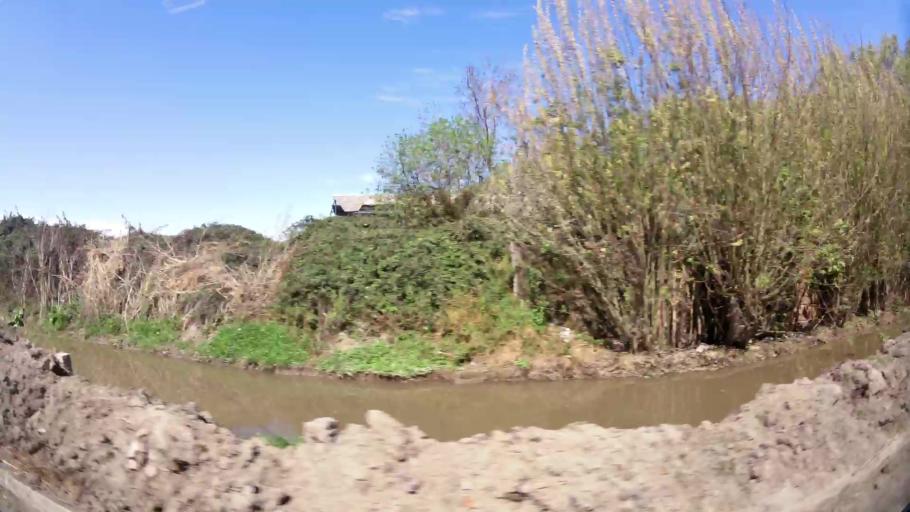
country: CL
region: Santiago Metropolitan
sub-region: Provincia de Talagante
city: Penaflor
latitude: -33.5965
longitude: -70.8815
